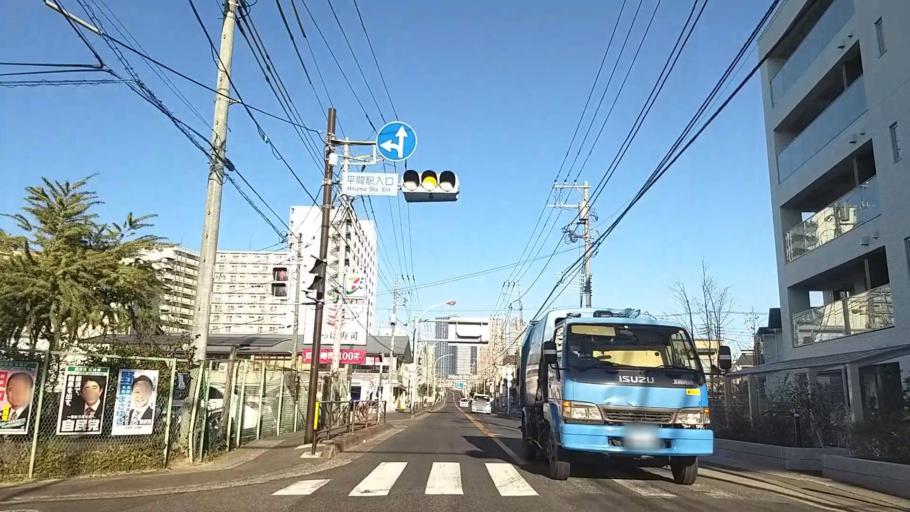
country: JP
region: Kanagawa
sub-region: Kawasaki-shi
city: Kawasaki
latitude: 35.5609
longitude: 139.6697
